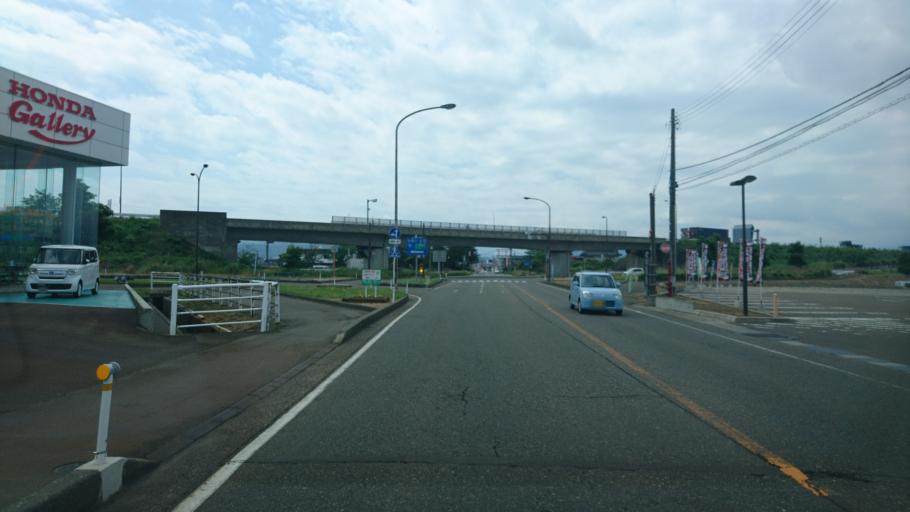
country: JP
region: Niigata
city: Arai
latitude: 37.0608
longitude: 138.2594
